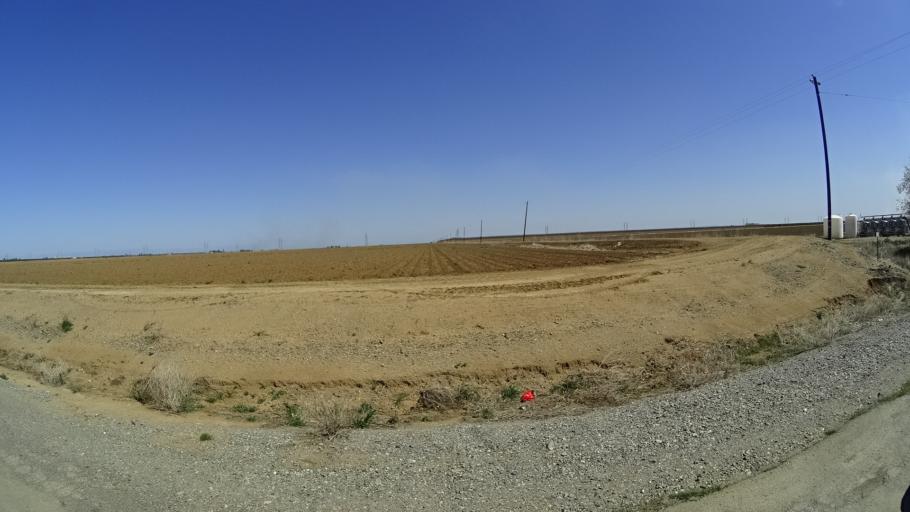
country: US
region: California
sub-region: Glenn County
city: Willows
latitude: 39.4805
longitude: -122.2772
